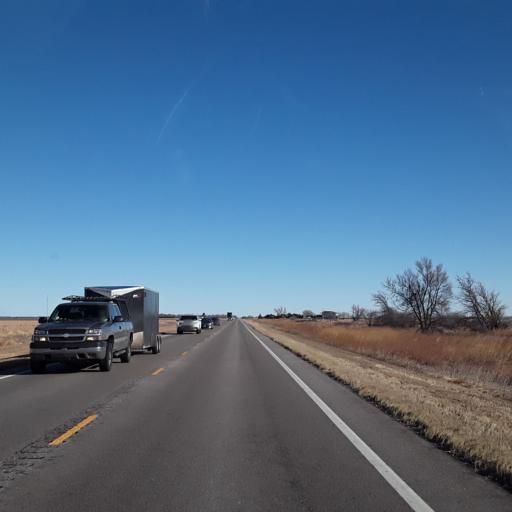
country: US
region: Kansas
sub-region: Pawnee County
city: Larned
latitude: 38.0980
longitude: -99.2110
